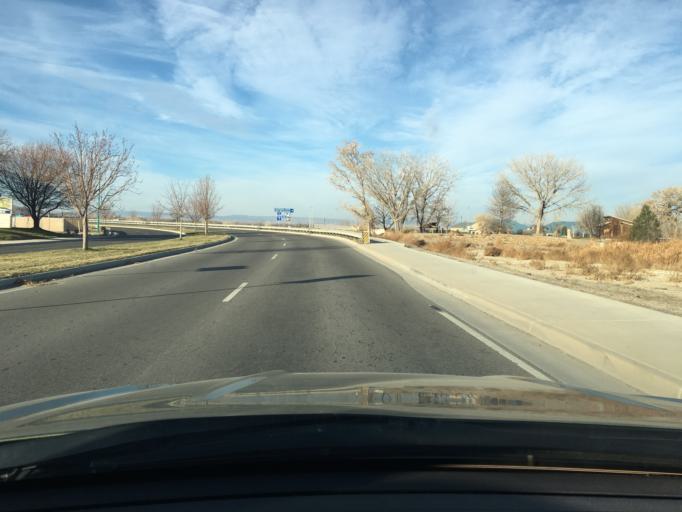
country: US
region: Colorado
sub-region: Delta County
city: Delta
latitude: 38.7489
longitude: -108.0726
